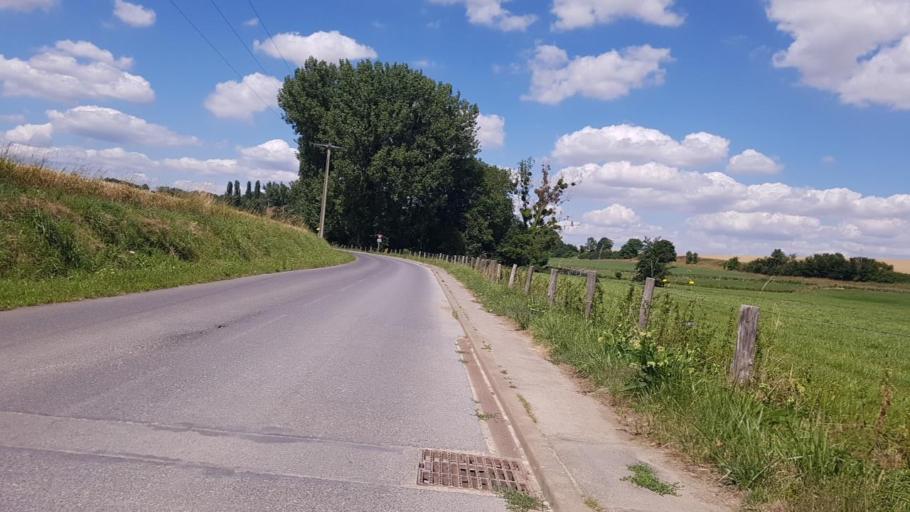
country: FR
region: Ile-de-France
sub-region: Departement de Seine-et-Marne
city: Juilly
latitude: 48.9878
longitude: 2.6694
